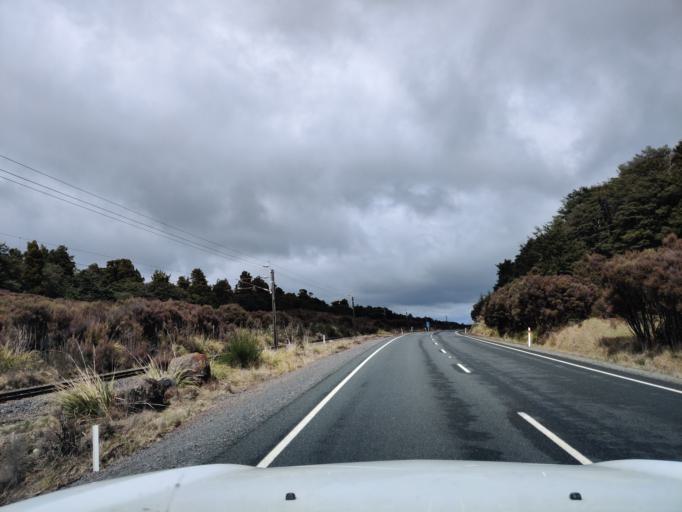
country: NZ
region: Manawatu-Wanganui
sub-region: Ruapehu District
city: Waiouru
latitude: -39.3074
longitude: 175.3899
